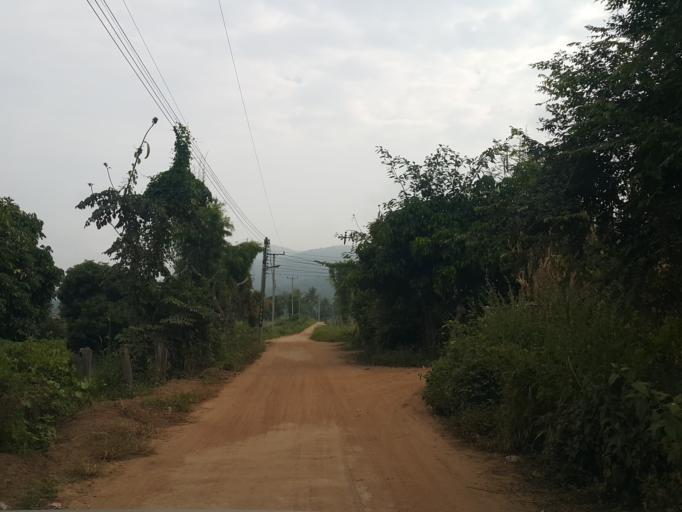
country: TH
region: Mae Hong Son
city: Wiang Nuea
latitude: 19.3762
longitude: 98.4524
